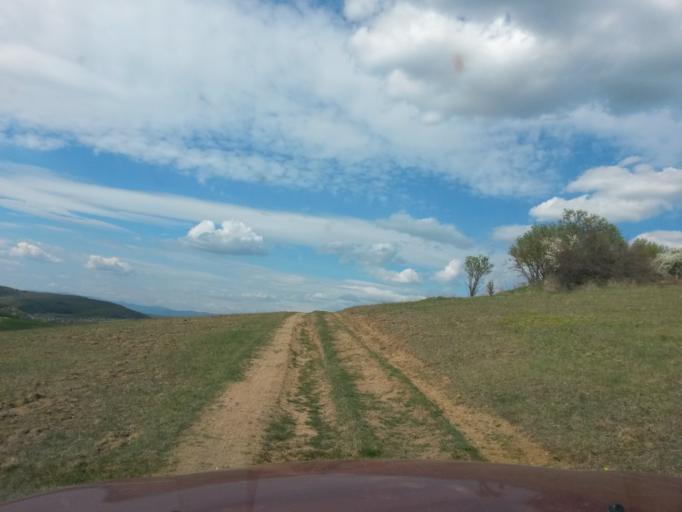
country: SK
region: Presovsky
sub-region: Okres Presov
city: Presov
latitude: 48.9539
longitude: 21.1282
